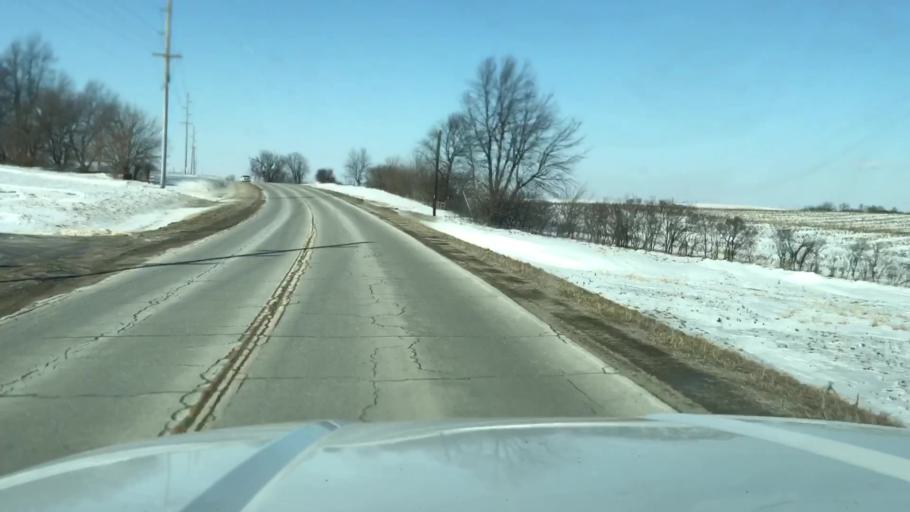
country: US
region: Missouri
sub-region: Andrew County
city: Savannah
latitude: 39.9588
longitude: -94.8521
